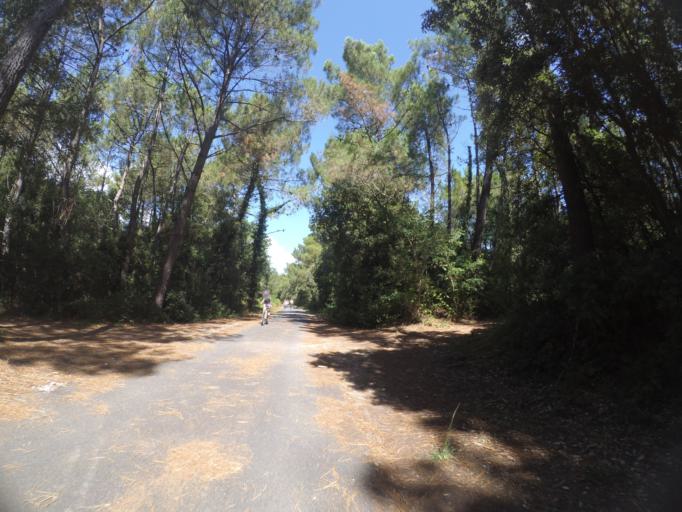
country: FR
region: Poitou-Charentes
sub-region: Departement de la Charente-Maritime
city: Les Mathes
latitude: 45.6760
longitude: -1.1518
